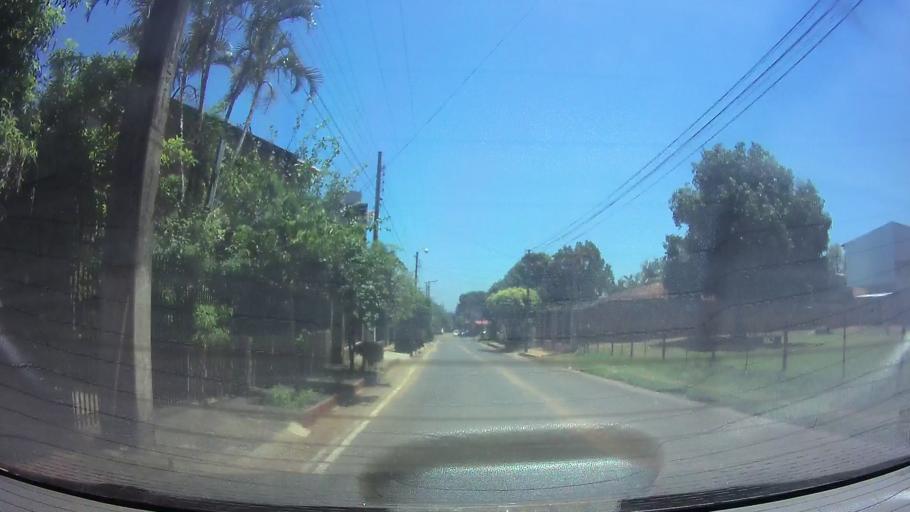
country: PY
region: Central
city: San Lorenzo
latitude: -25.3338
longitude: -57.4845
